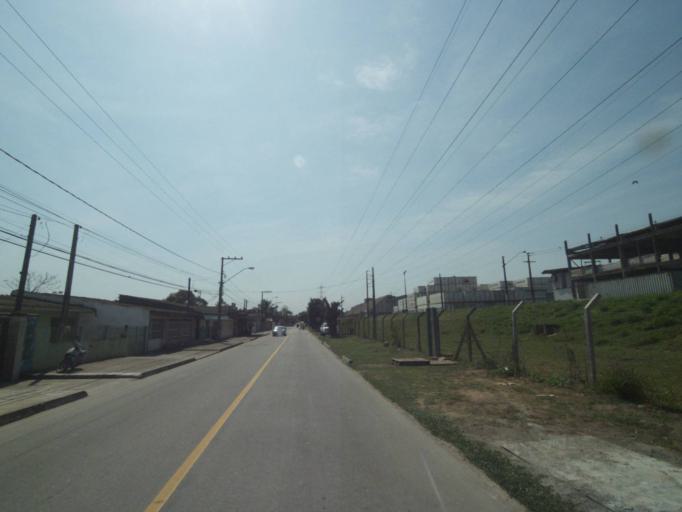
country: BR
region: Parana
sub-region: Paranagua
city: Paranagua
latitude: -25.5407
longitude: -48.5444
